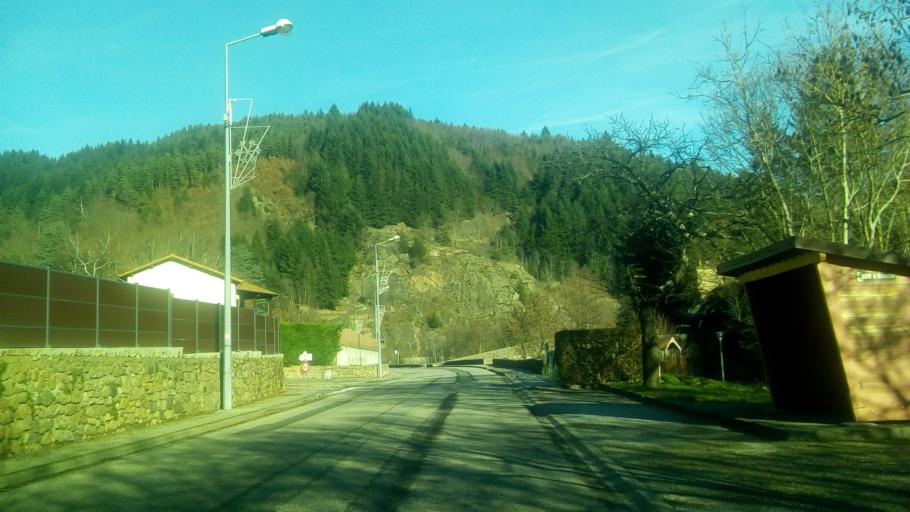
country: FR
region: Rhone-Alpes
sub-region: Departement de l'Ardeche
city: Saint-Martin-de-Valamas
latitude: 44.8894
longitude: 4.3770
